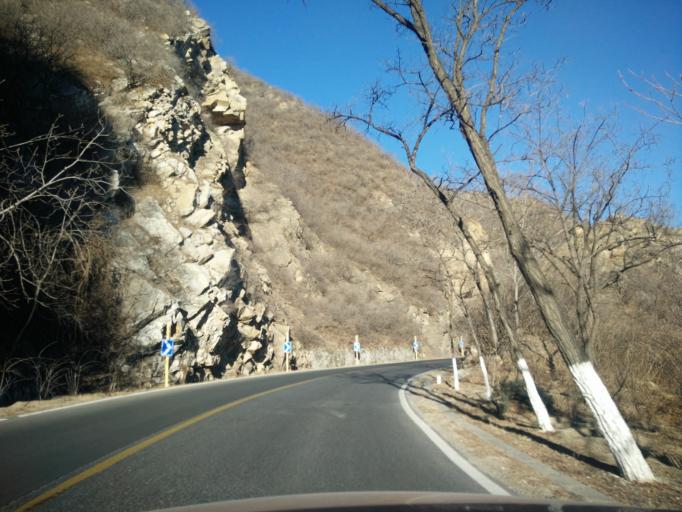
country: CN
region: Beijing
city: Wangping
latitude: 40.0059
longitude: 115.9792
